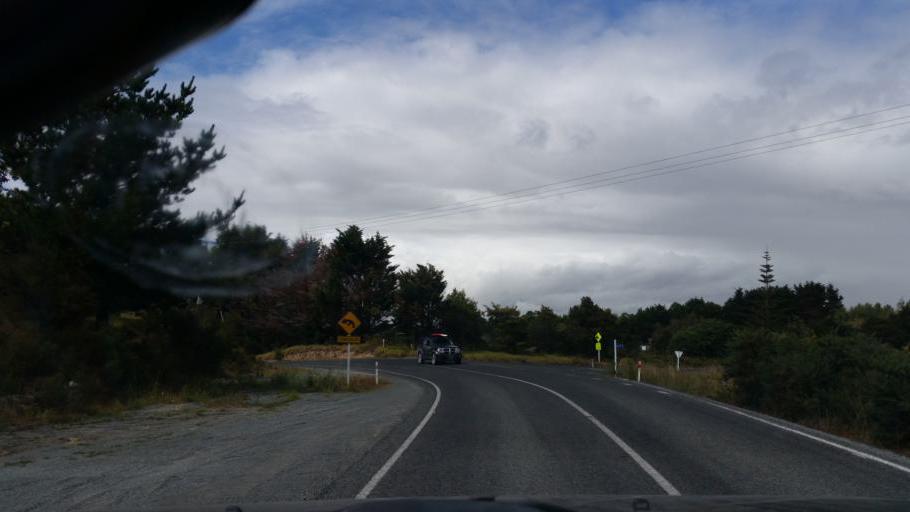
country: NZ
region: Auckland
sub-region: Auckland
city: Wellsford
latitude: -36.1137
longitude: 174.5408
